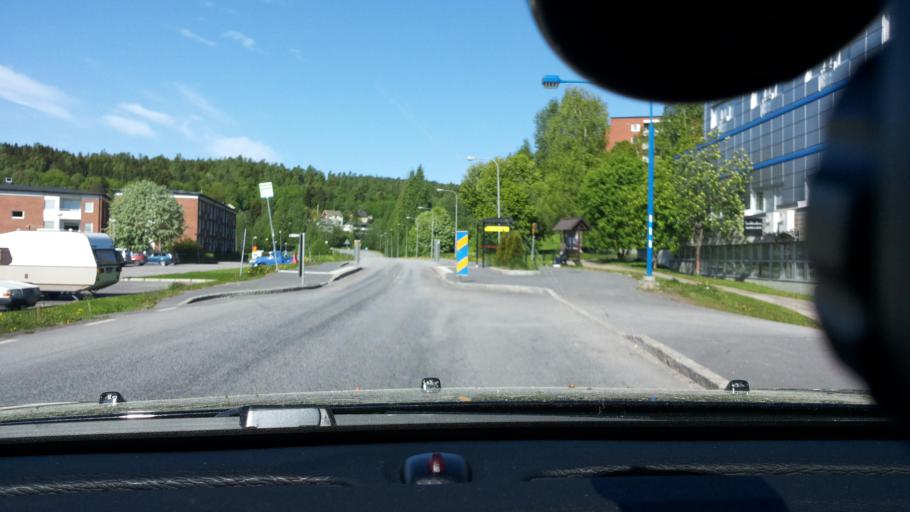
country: SE
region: Vaesternorrland
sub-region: Sundsvalls Kommun
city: Sundsbruk
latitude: 62.4584
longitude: 17.3554
